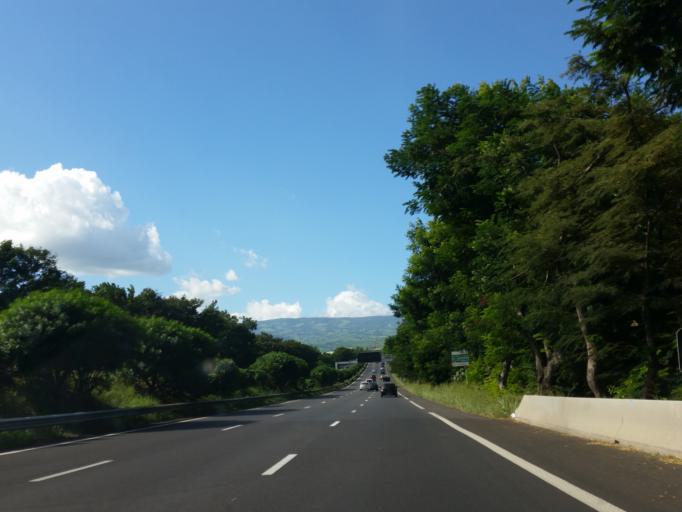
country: RE
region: Reunion
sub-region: Reunion
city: Saint-Pierre
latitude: -21.3328
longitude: 55.4629
